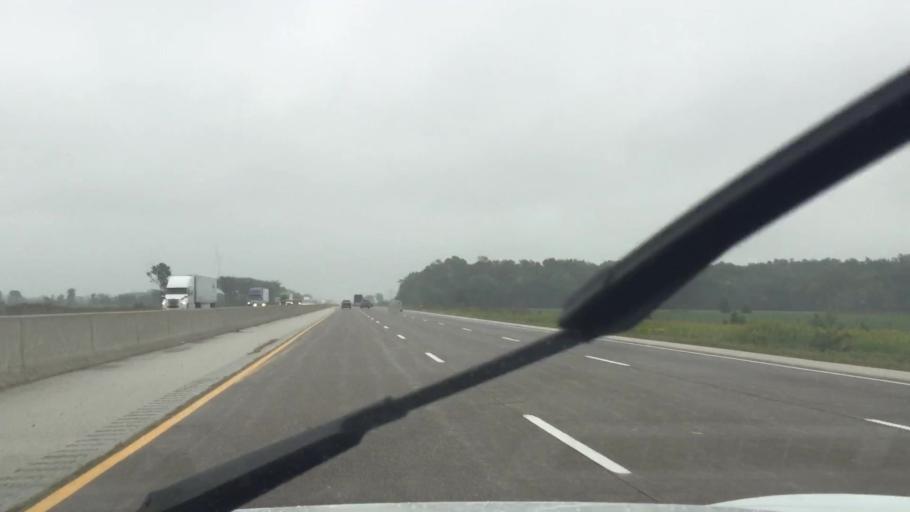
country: US
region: Michigan
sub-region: Wayne County
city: Grosse Pointe
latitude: 42.2376
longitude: -82.7531
